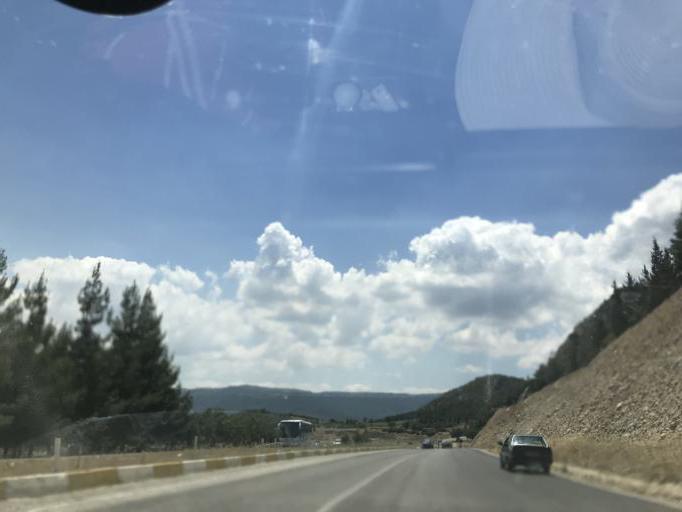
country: TR
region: Denizli
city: Honaz
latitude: 37.7027
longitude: 29.2016
